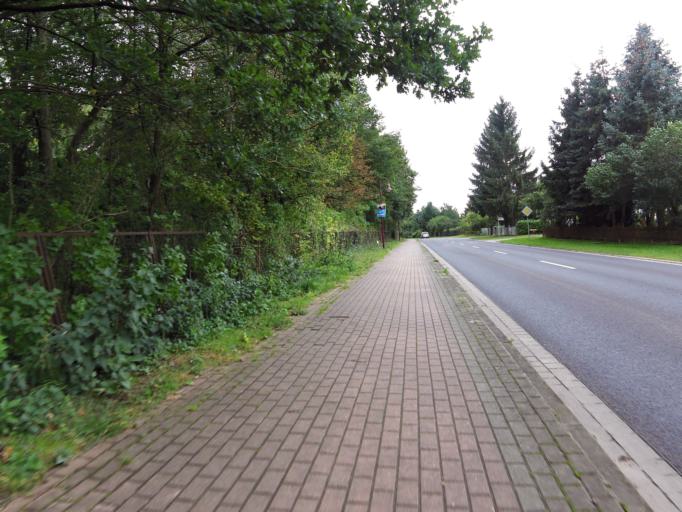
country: DE
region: Saxony-Anhalt
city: Schonhausen
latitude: 52.6168
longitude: 11.9994
